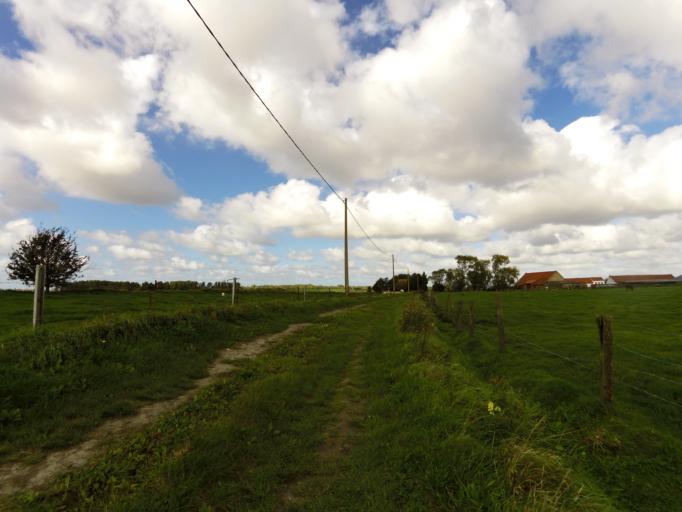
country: BE
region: Flanders
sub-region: Provincie West-Vlaanderen
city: Ostend
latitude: 51.1928
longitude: 2.9315
